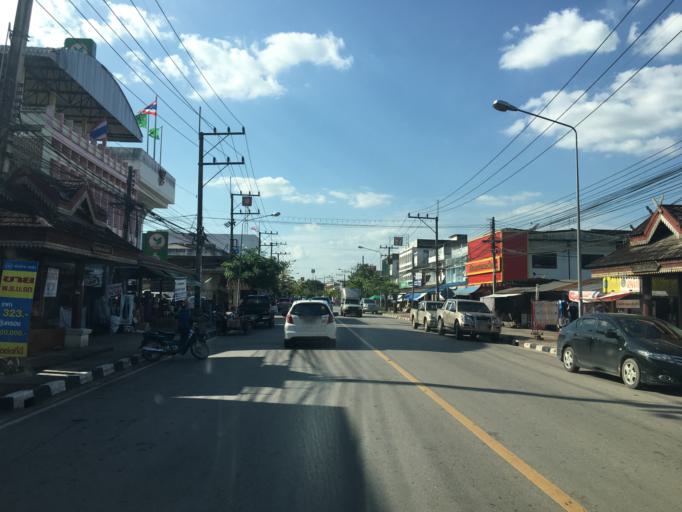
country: TH
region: Phayao
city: Chun
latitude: 19.3400
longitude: 100.1260
